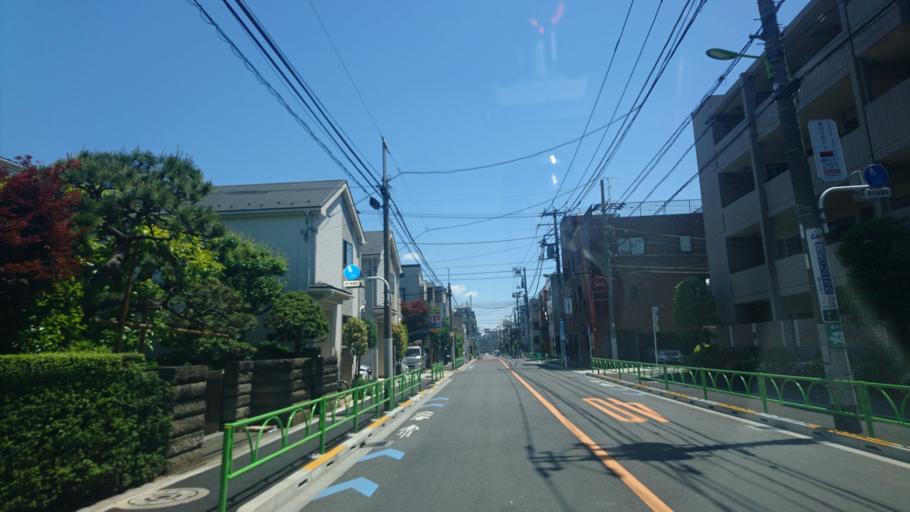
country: JP
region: Tokyo
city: Tokyo
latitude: 35.6476
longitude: 139.6277
